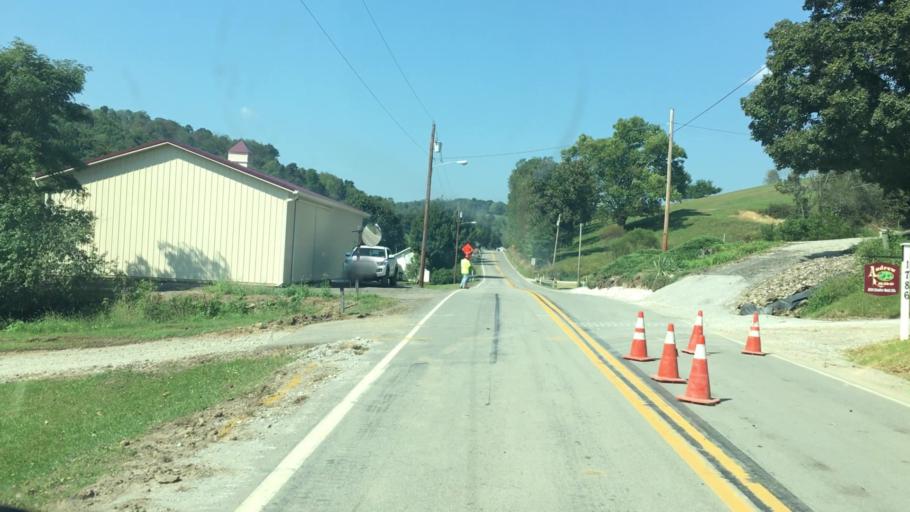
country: US
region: Pennsylvania
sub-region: Greene County
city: Waynesburg
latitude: 39.9628
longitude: -80.3104
